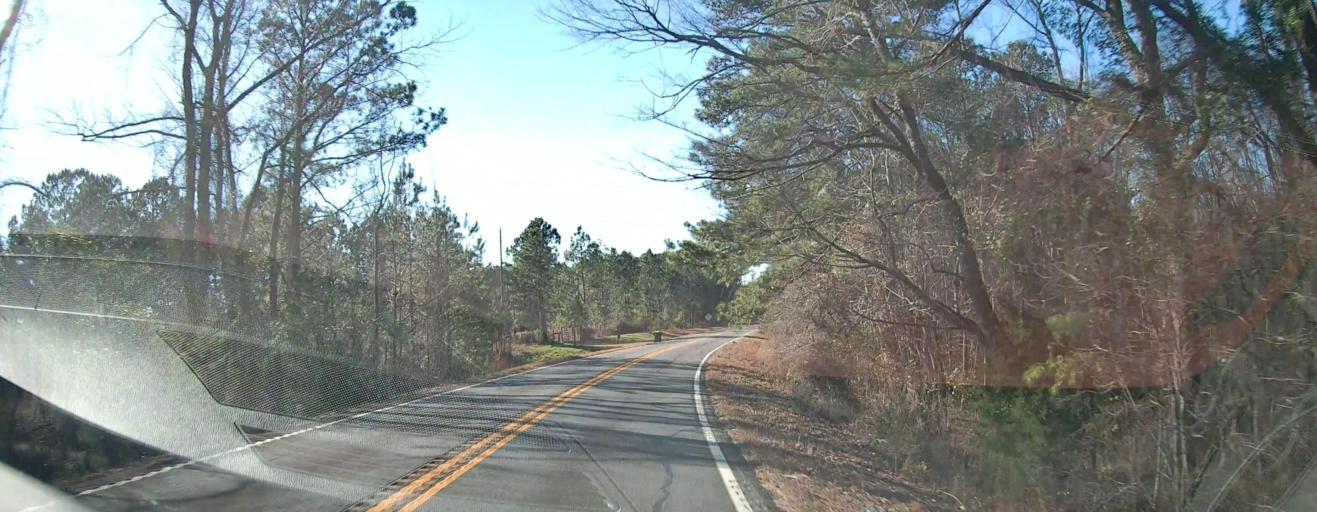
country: US
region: Georgia
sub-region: Talbot County
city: Talbotton
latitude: 32.6458
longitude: -84.4372
